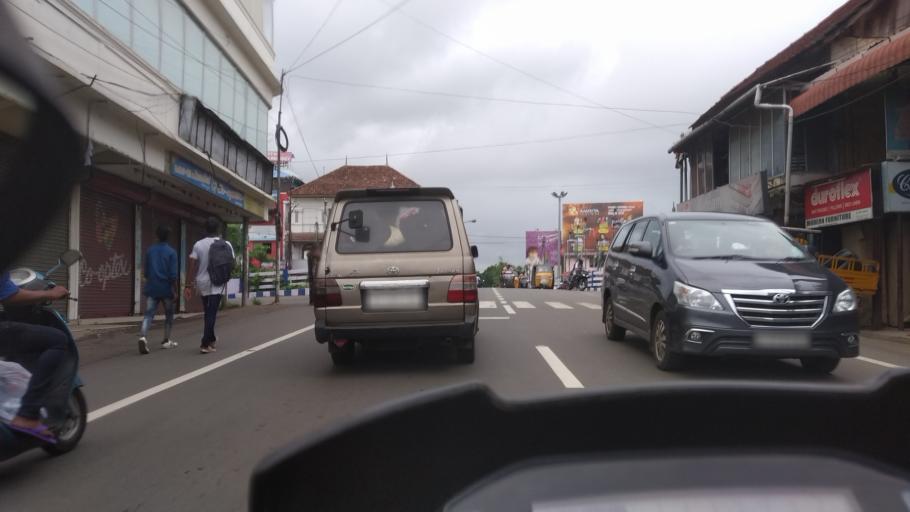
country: IN
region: Kerala
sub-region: Alappuzha
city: Alleppey
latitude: 9.4950
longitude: 76.3388
